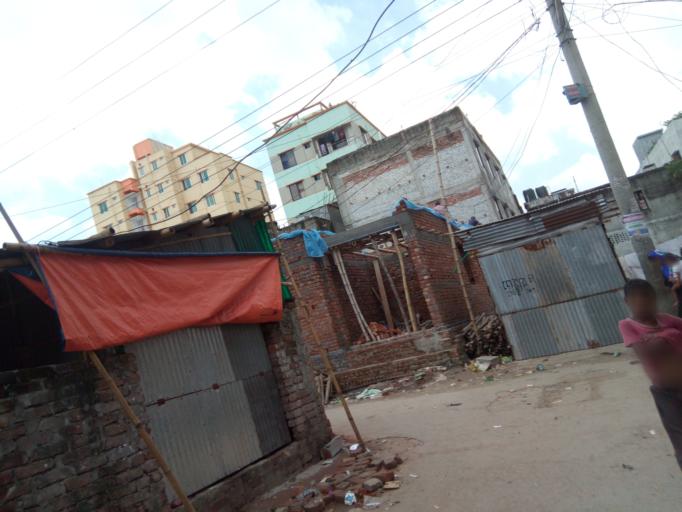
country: BD
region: Dhaka
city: Azimpur
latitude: 23.7462
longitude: 90.3610
